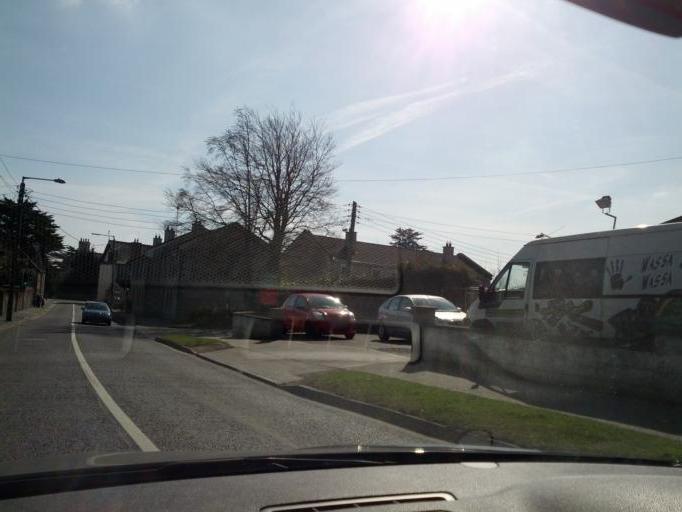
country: IE
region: Leinster
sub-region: Kildare
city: Celbridge
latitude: 53.3421
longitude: -6.5386
